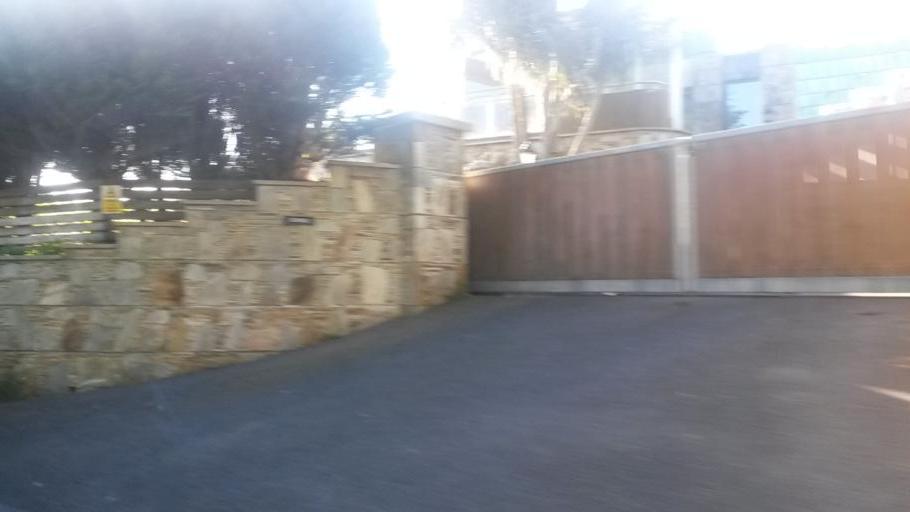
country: IE
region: Leinster
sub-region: Fingal County
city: Howth
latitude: 53.3695
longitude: -6.0657
